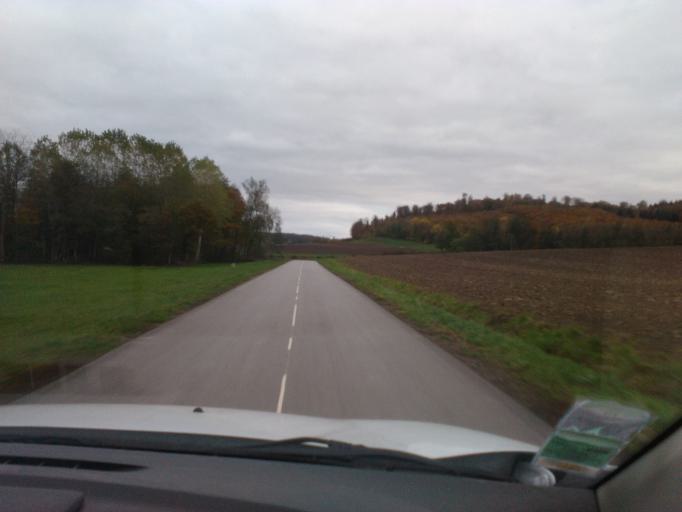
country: FR
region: Lorraine
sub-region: Departement des Vosges
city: Vincey
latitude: 48.2743
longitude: 6.2438
